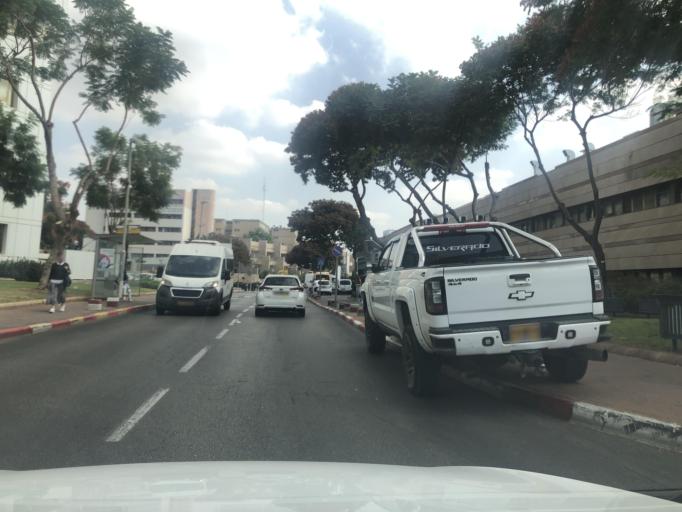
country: IL
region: Tel Aviv
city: Or Yehuda
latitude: 32.0474
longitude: 34.8436
